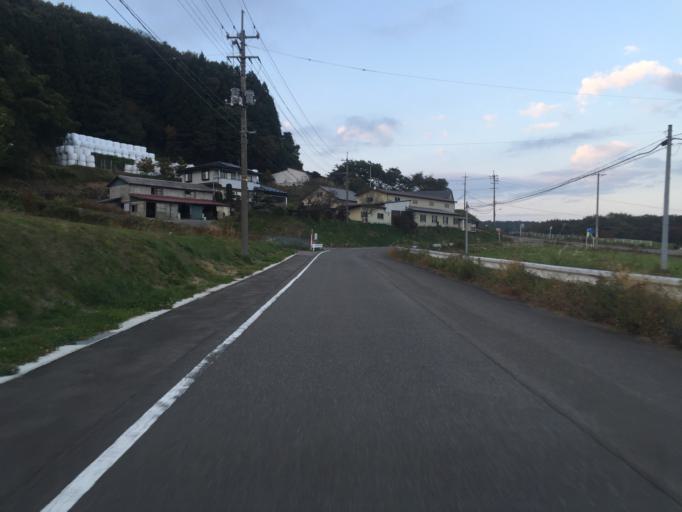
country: JP
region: Fukushima
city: Nihommatsu
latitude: 37.6129
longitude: 140.3574
